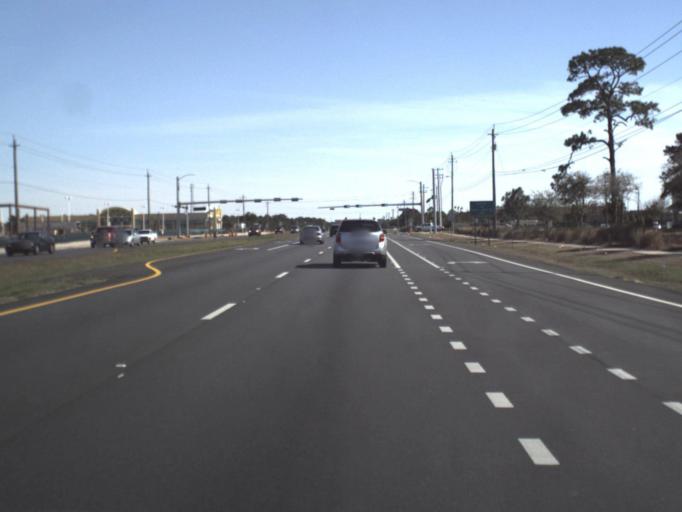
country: US
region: Florida
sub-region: Bay County
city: Laguna Beach
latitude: 30.2218
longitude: -85.8677
